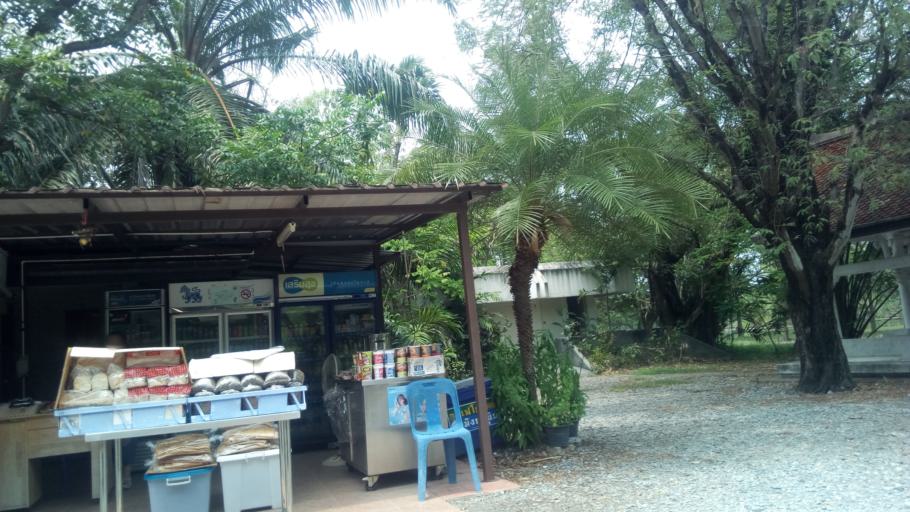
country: TH
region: Bangkok
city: Thawi Watthana
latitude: 13.7787
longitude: 100.3174
